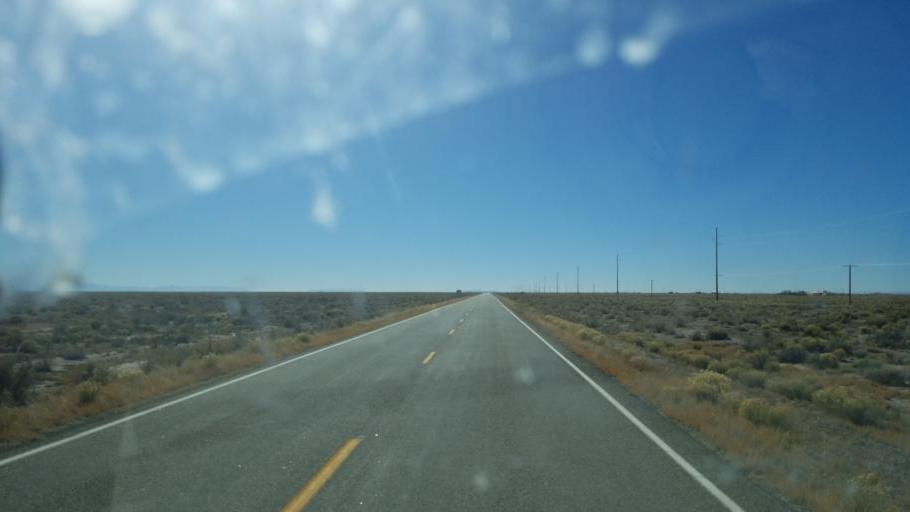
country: US
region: Colorado
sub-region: Saguache County
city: Center
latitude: 37.8650
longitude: -105.8935
